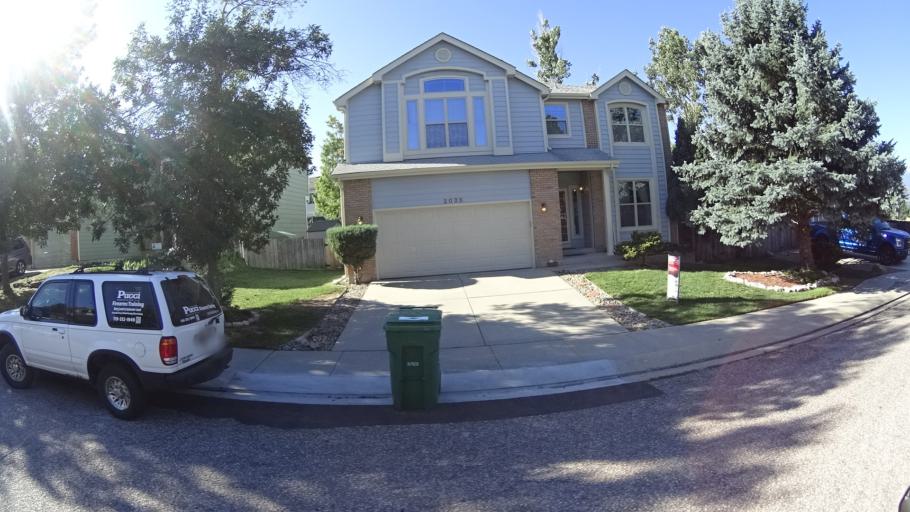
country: US
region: Colorado
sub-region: El Paso County
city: Air Force Academy
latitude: 38.9725
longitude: -104.7923
